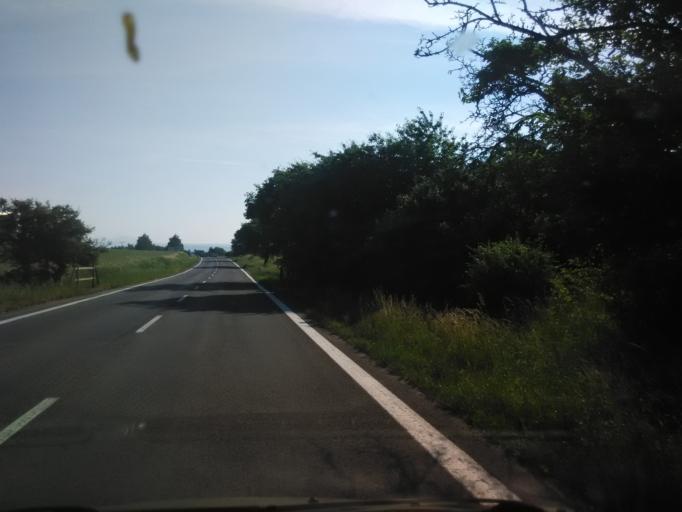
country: SK
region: Nitriansky
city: Levice
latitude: 48.2582
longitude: 18.6998
